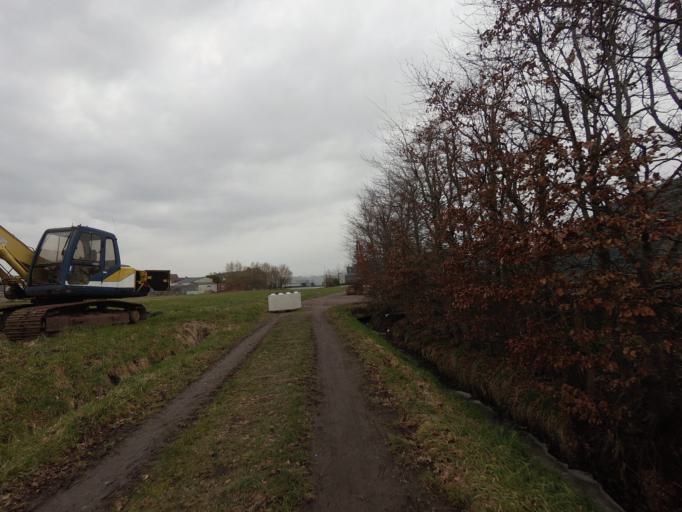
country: BE
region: Flanders
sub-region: Provincie Antwerpen
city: Aartselaar
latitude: 51.1353
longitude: 4.3723
